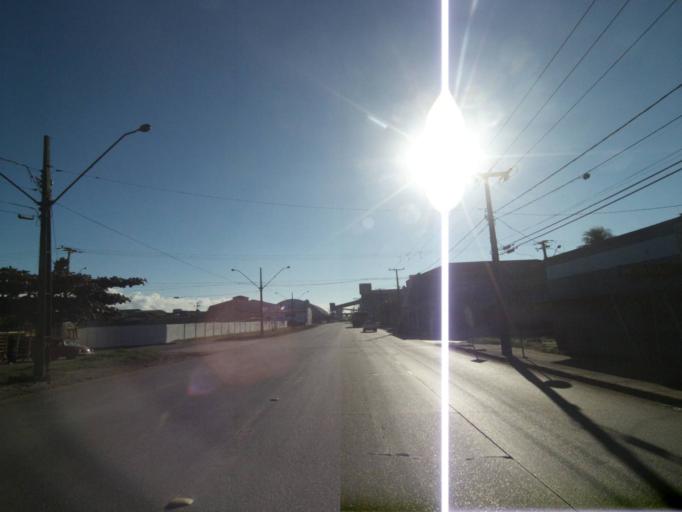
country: BR
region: Parana
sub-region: Paranagua
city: Paranagua
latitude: -25.5117
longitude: -48.5201
